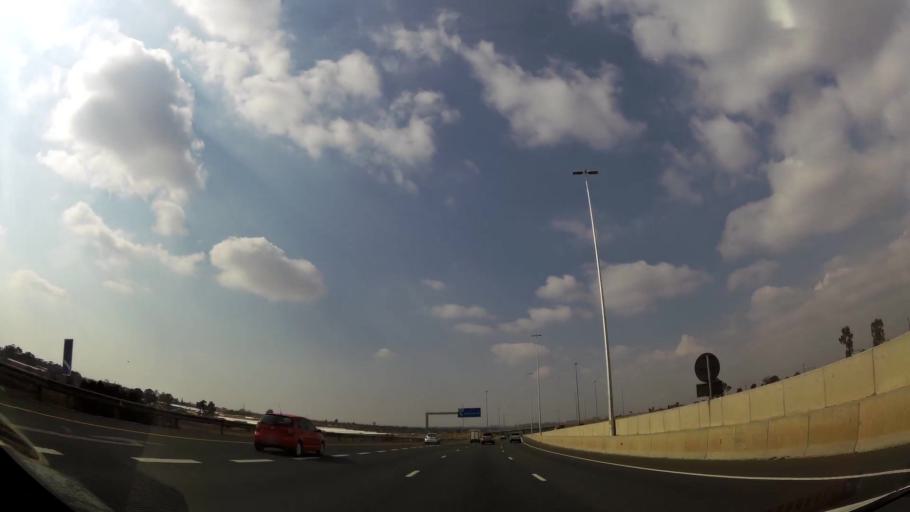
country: ZA
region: Gauteng
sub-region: Ekurhuleni Metropolitan Municipality
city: Benoni
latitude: -26.1630
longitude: 28.3648
